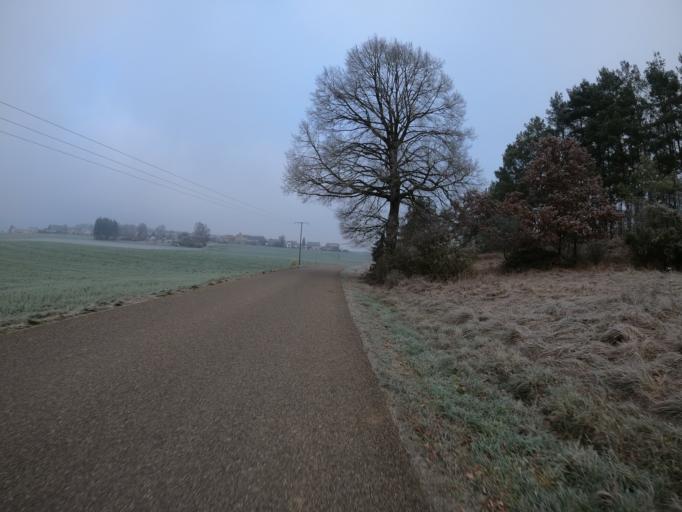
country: DE
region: Baden-Wuerttemberg
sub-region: Tuebingen Region
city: Westerstetten
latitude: 48.4999
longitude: 9.9508
